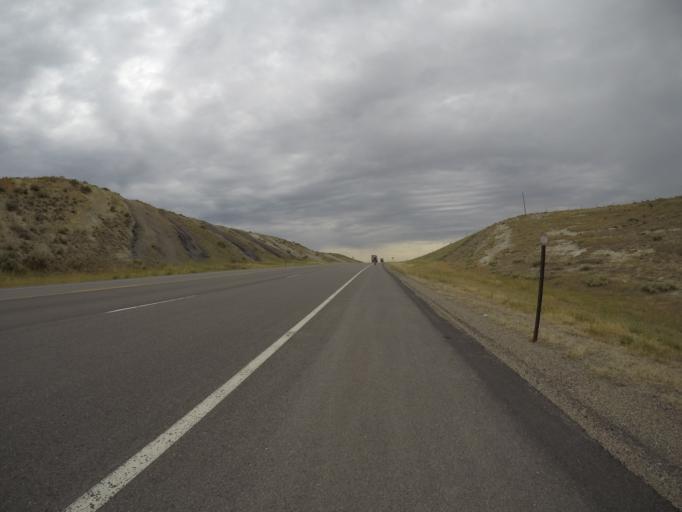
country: US
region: Wyoming
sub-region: Lincoln County
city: Kemmerer
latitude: 41.8054
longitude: -110.6045
